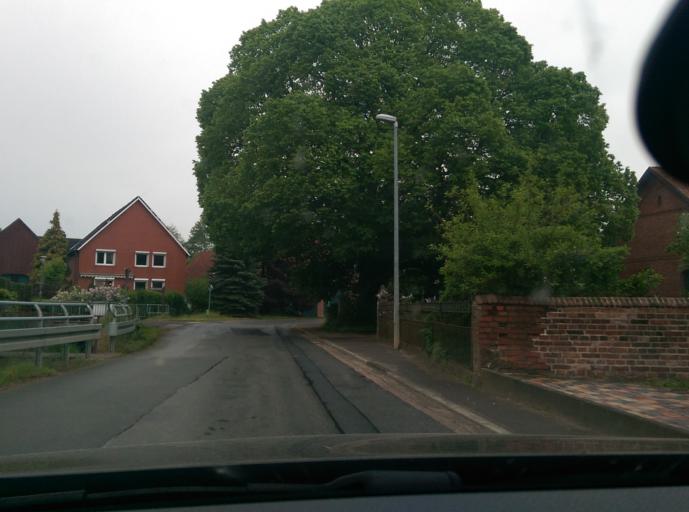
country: DE
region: Lower Saxony
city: Pohle
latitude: 52.2621
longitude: 9.3366
